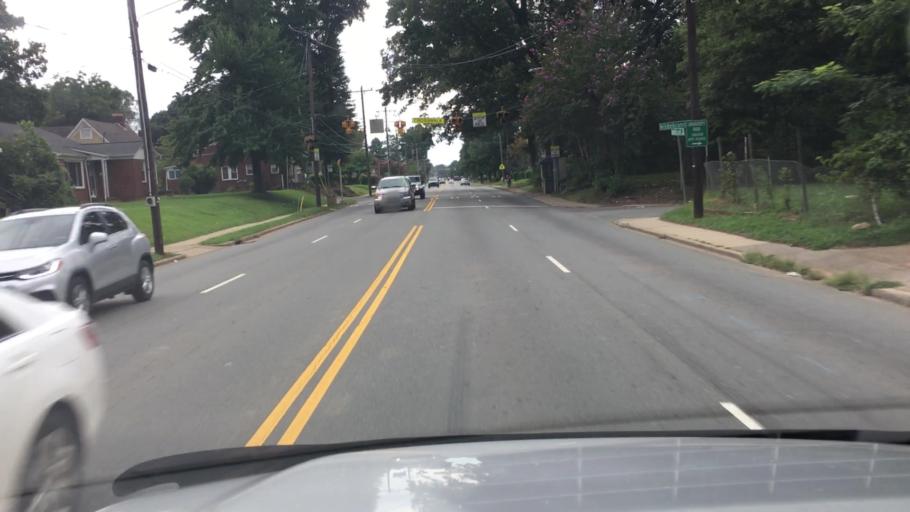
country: US
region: North Carolina
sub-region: Mecklenburg County
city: Charlotte
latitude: 35.2607
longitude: -80.8551
